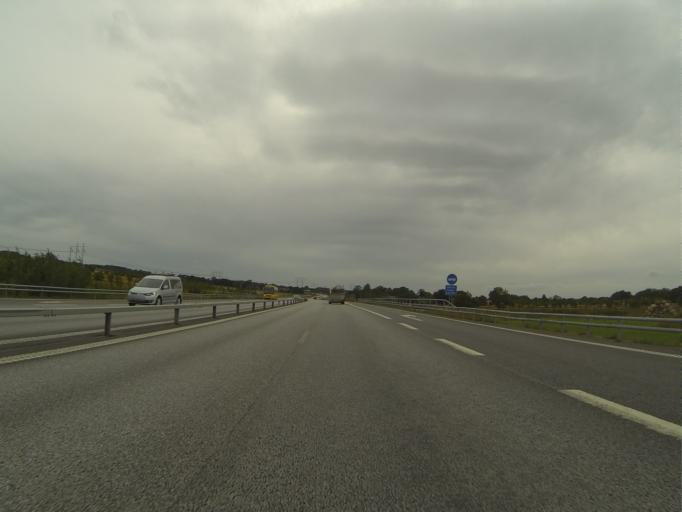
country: SE
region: Skane
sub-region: Hoors Kommun
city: Loberod
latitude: 55.8074
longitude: 13.4702
